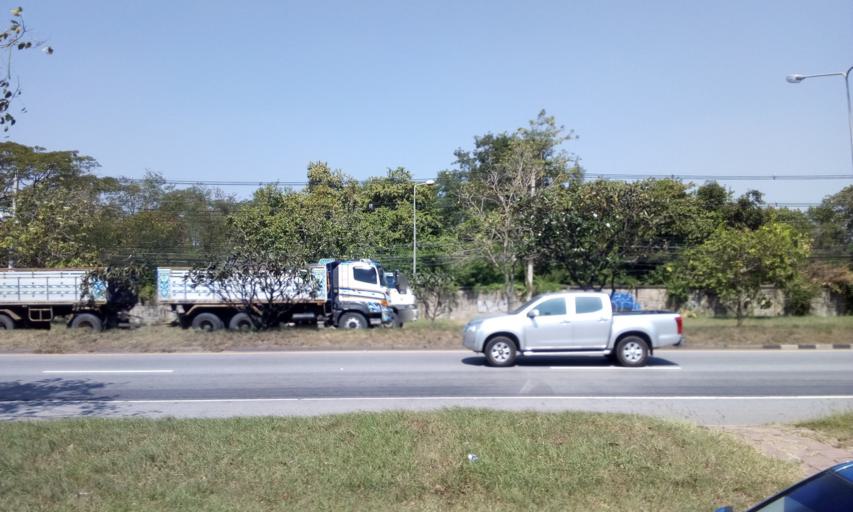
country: TH
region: Nakhon Ratchasima
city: Sikhio
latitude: 14.8679
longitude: 101.7208
